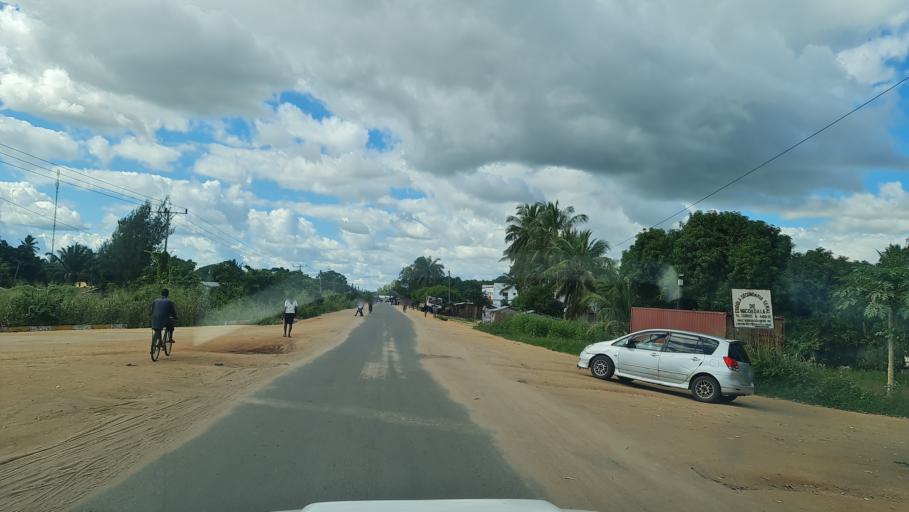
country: MZ
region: Zambezia
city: Quelimane
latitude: -17.5983
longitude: 36.8089
